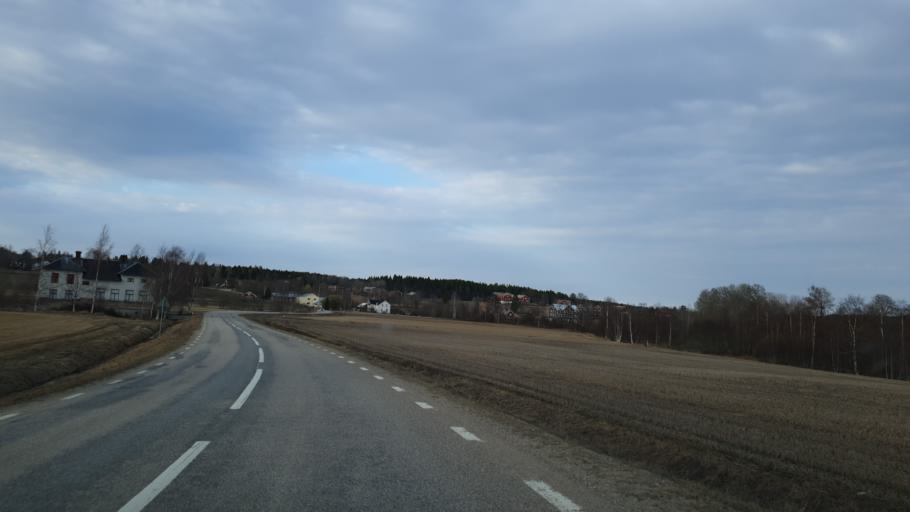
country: SE
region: Gaevleborg
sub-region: Nordanstigs Kommun
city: Bergsjoe
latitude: 61.9753
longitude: 17.2609
